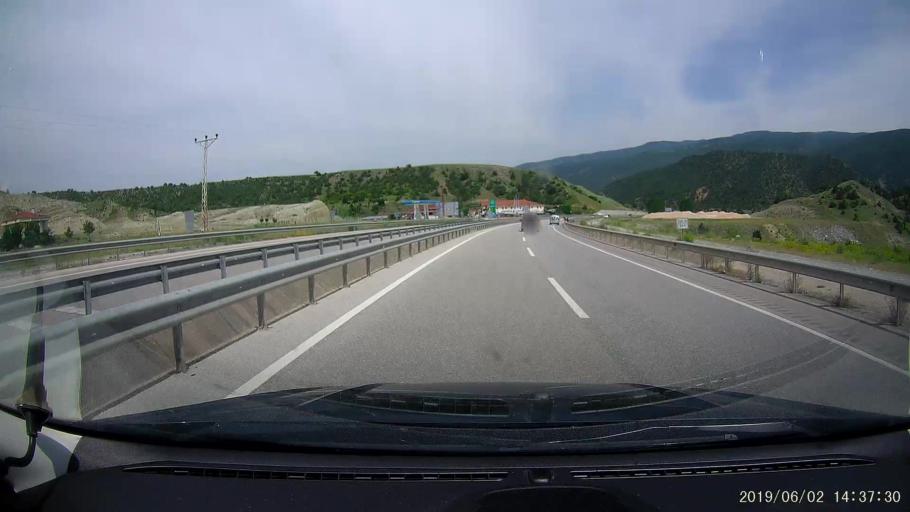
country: TR
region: Corum
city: Hacihamza
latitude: 41.0525
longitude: 34.2593
